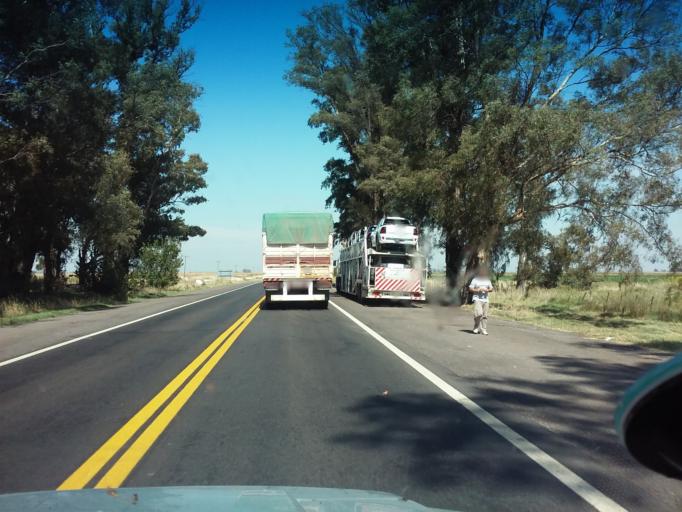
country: AR
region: Buenos Aires
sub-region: Partido de Nueve de Julio
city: Nueve de Julio
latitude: -35.3631
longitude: -60.7059
